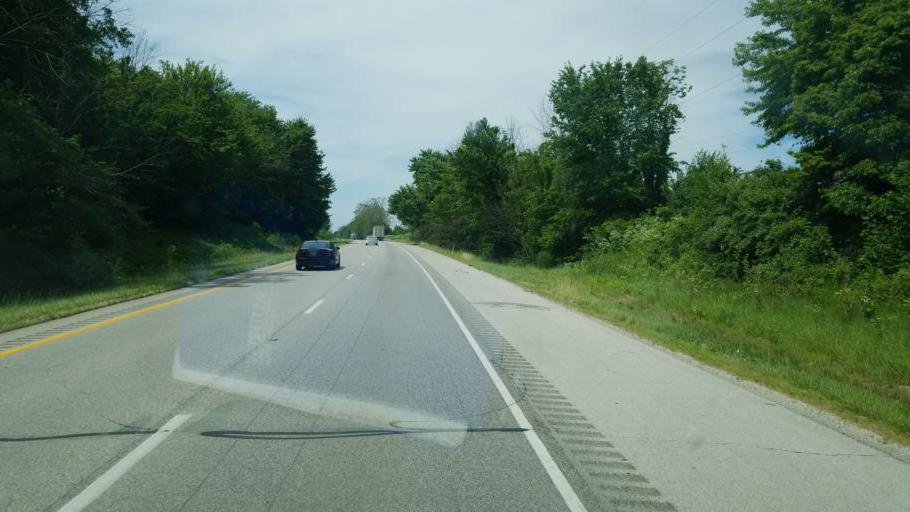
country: US
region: Indiana
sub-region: Vigo County
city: Seelyville
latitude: 39.4425
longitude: -87.2744
